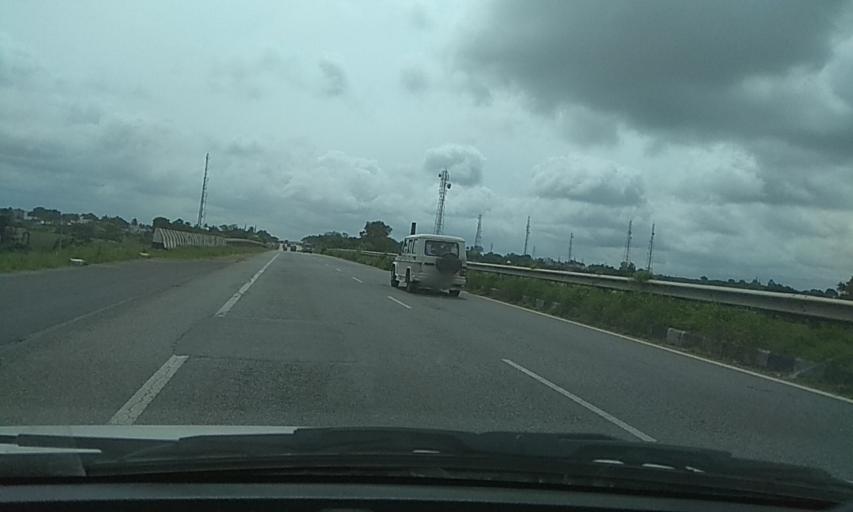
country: IN
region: Karnataka
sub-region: Davanagere
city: Mayakonda
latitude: 14.3950
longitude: 76.0377
